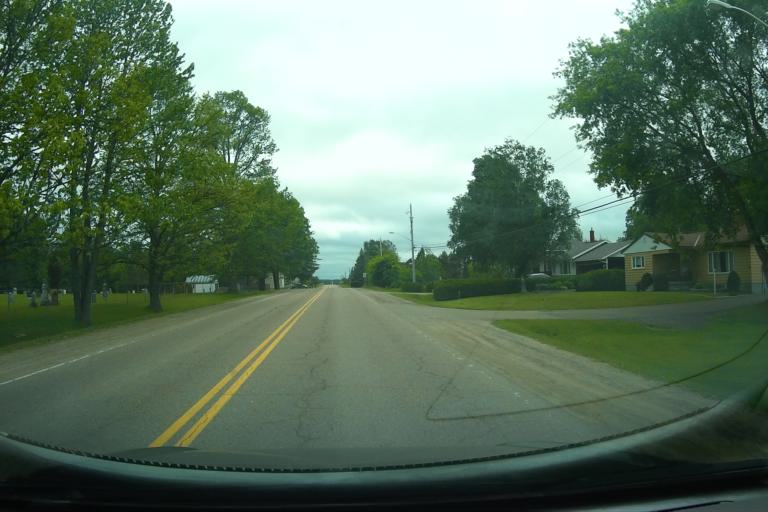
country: CA
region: Ontario
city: Pembroke
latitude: 45.5316
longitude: -77.0986
